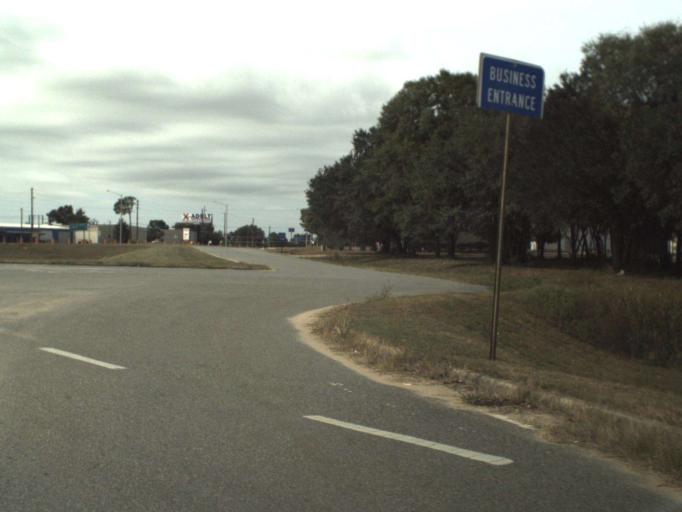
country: US
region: Florida
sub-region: Leon County
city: Tallahassee
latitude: 30.4379
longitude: -84.3495
